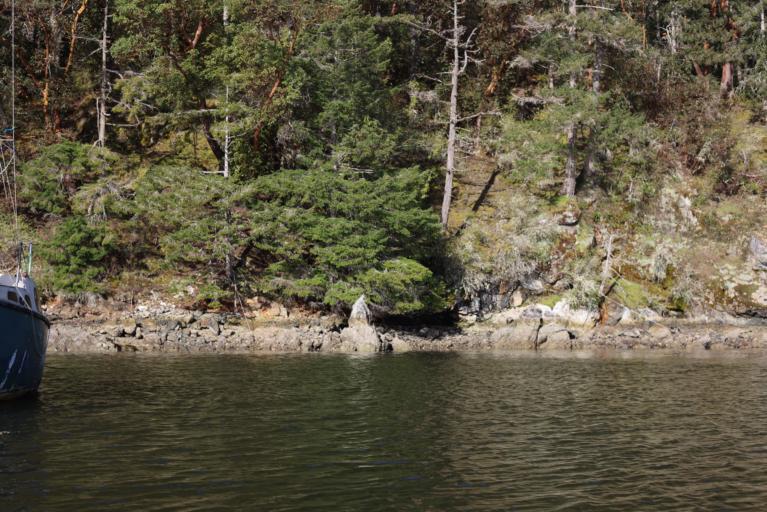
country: CA
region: British Columbia
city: North Saanich
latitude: 48.5701
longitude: -123.4744
